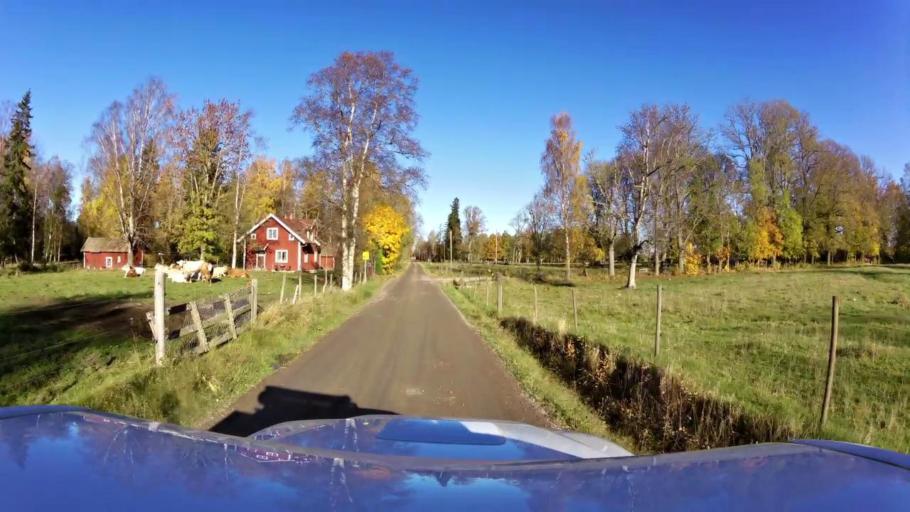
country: SE
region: OEstergoetland
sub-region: Linkopings Kommun
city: Vikingstad
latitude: 58.4840
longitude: 15.3890
